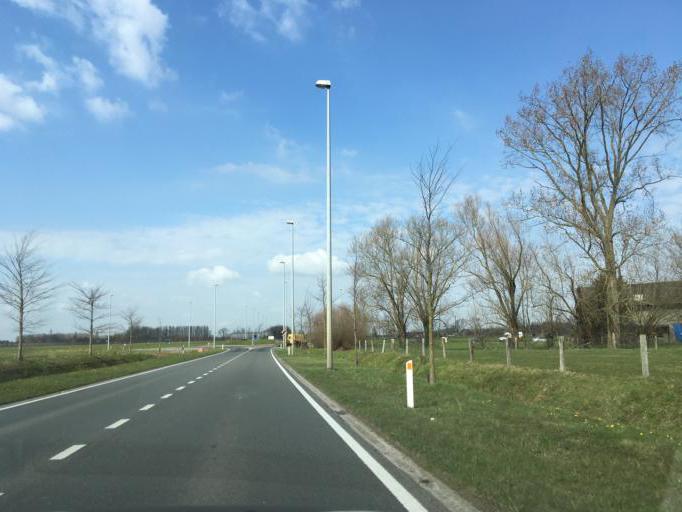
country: BE
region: Flanders
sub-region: Provincie West-Vlaanderen
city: Kuurne
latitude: 50.8690
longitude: 3.2932
